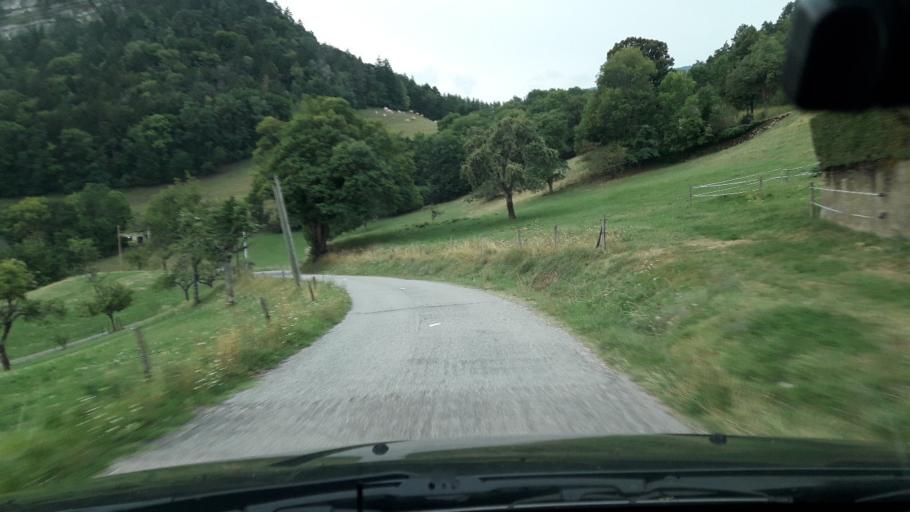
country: FR
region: Rhone-Alpes
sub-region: Departement de la Savoie
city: Barberaz
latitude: 45.5400
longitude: 5.9296
